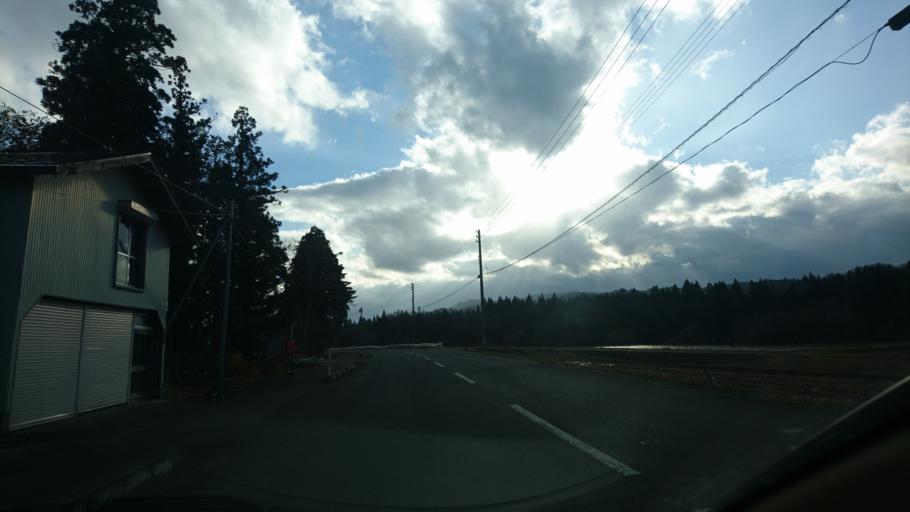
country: JP
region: Akita
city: Yokotemachi
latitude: 39.3876
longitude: 140.7655
